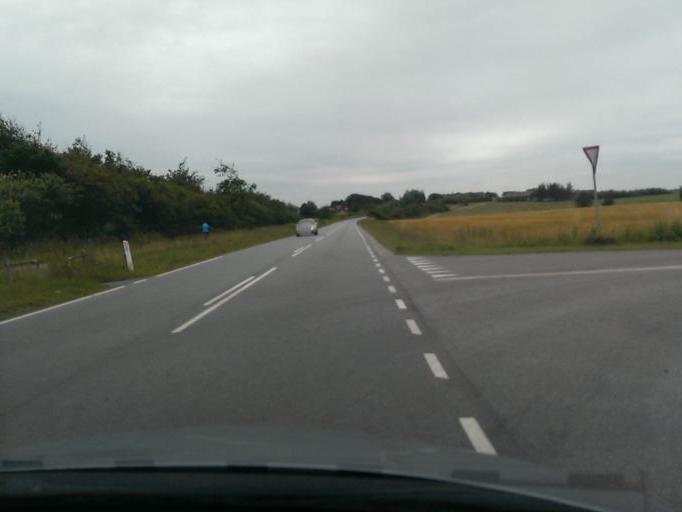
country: DK
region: North Denmark
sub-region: Hjorring Kommune
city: Vra
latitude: 57.3549
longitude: 9.9187
